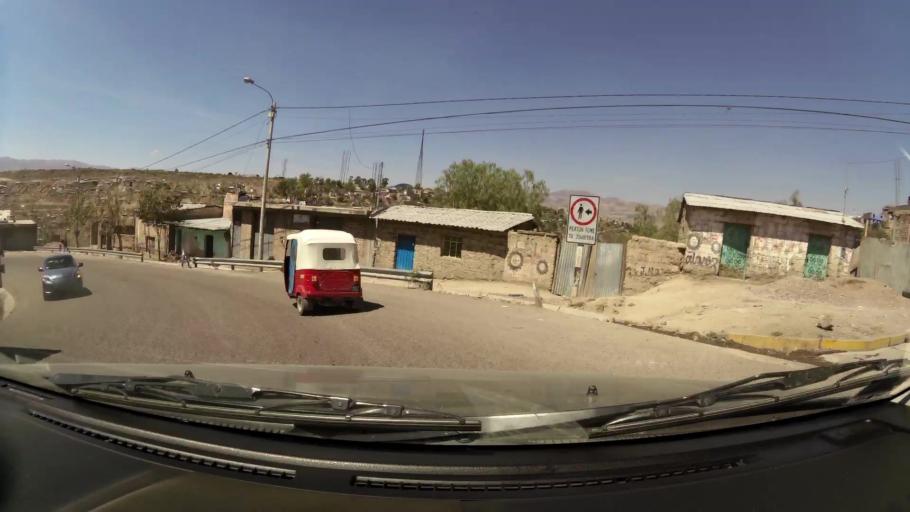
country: PE
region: Ayacucho
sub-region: Provincia de Huamanga
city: Ayacucho
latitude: -13.1470
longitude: -74.2118
